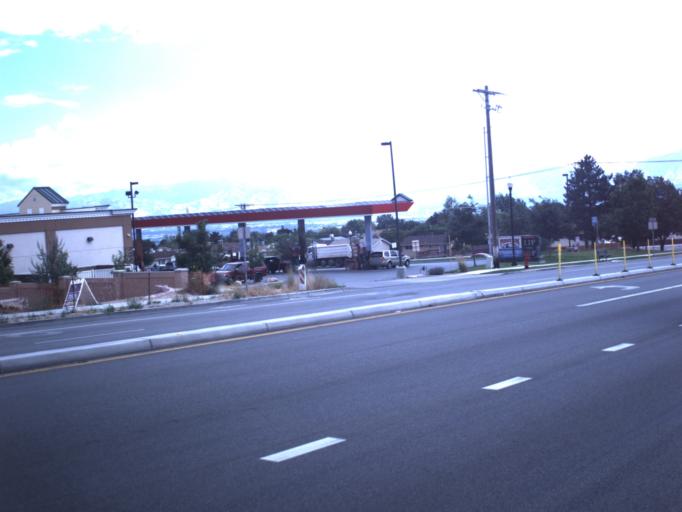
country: US
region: Utah
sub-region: Salt Lake County
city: Oquirrh
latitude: 40.6530
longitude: -112.0261
